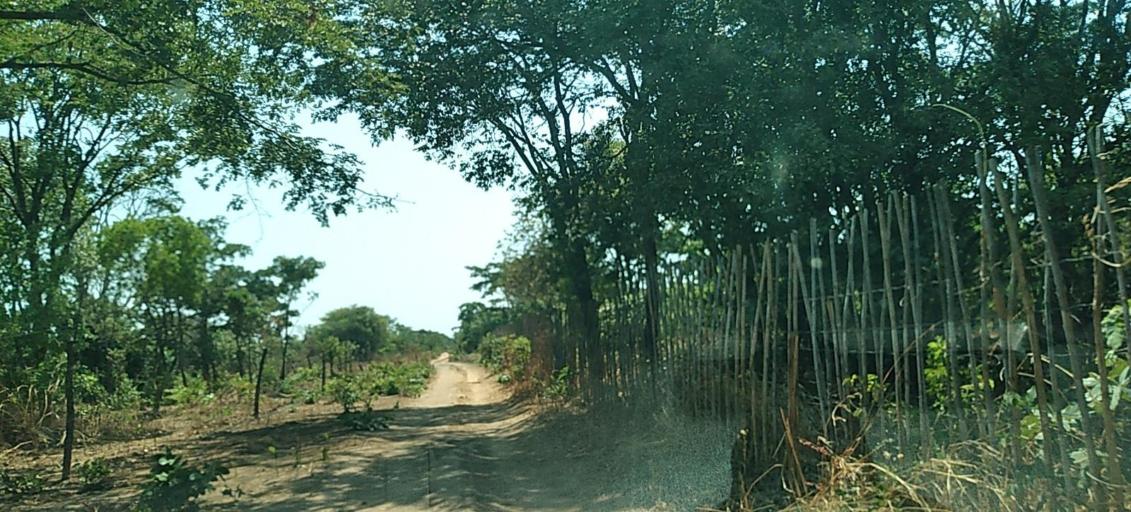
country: ZM
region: Copperbelt
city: Luanshya
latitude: -13.0084
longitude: 28.4713
